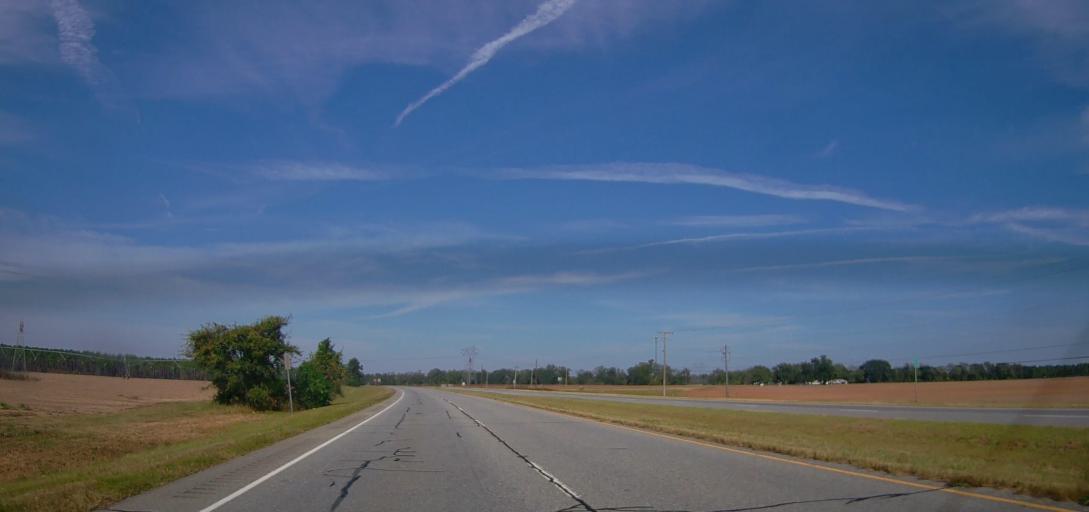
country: US
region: Georgia
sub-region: Dougherty County
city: Putney
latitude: 31.3599
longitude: -84.1562
